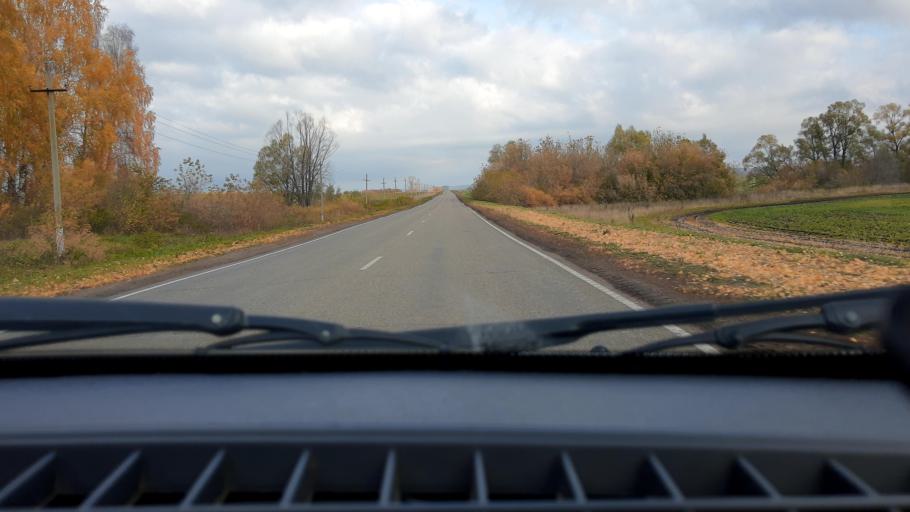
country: RU
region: Bashkortostan
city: Ulukulevo
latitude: 54.4005
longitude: 56.3778
